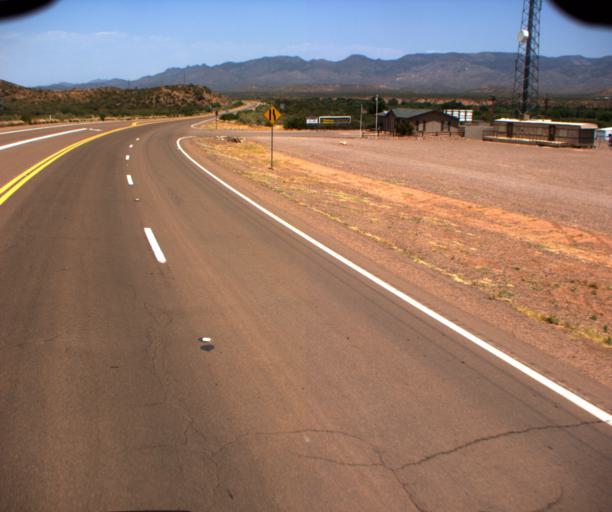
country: US
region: Arizona
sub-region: Gila County
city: Tonto Basin
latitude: 33.8774
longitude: -111.3156
